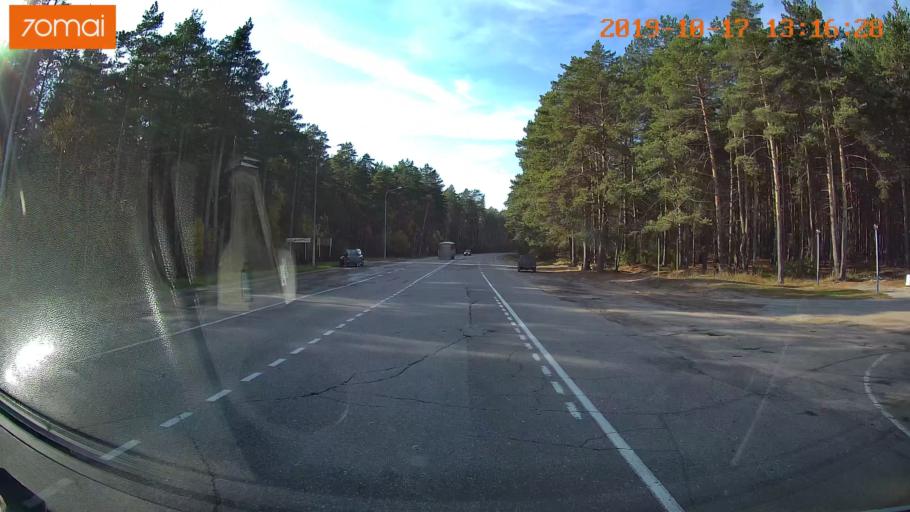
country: RU
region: Rjazan
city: Gus'-Zheleznyy
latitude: 55.0493
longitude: 41.1397
